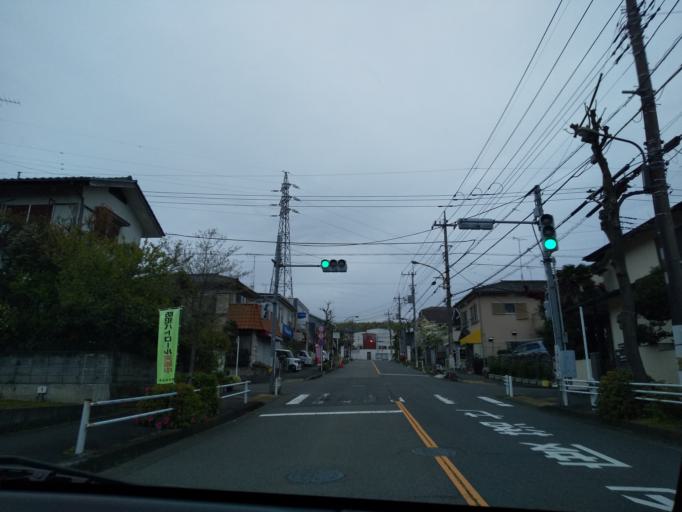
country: JP
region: Tokyo
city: Hino
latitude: 35.6326
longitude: 139.3745
